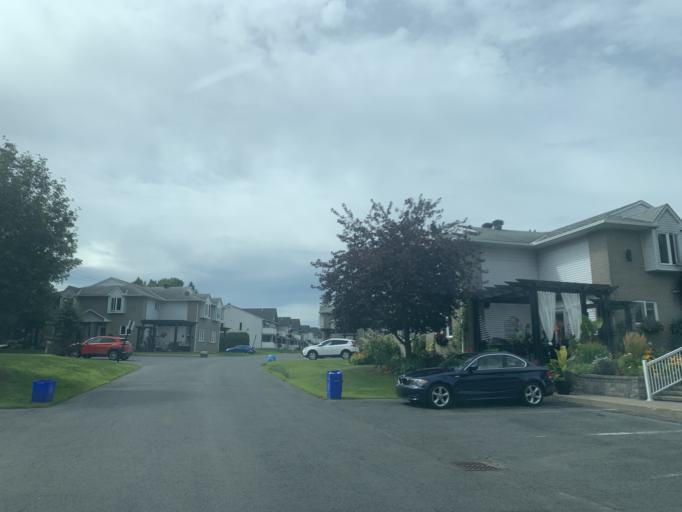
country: CA
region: Ontario
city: Hawkesbury
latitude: 45.6041
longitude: -74.6095
